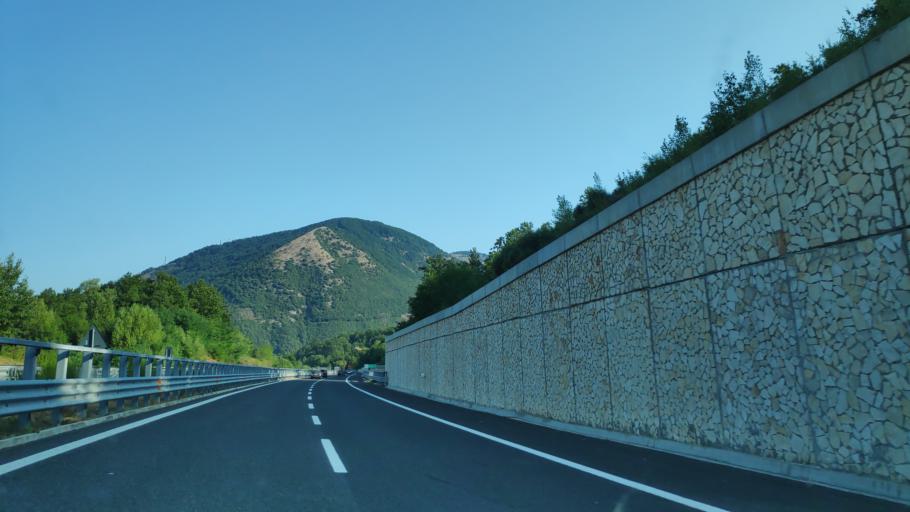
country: IT
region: Basilicate
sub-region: Provincia di Potenza
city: Lagonegro
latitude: 40.1167
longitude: 15.7850
